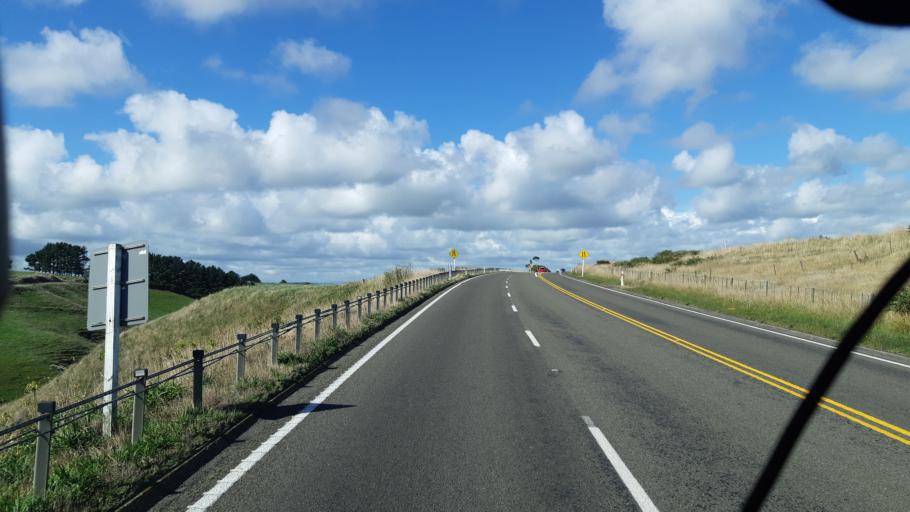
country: NZ
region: Manawatu-Wanganui
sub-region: Wanganui District
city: Wanganui
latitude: -40.0256
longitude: 175.1888
